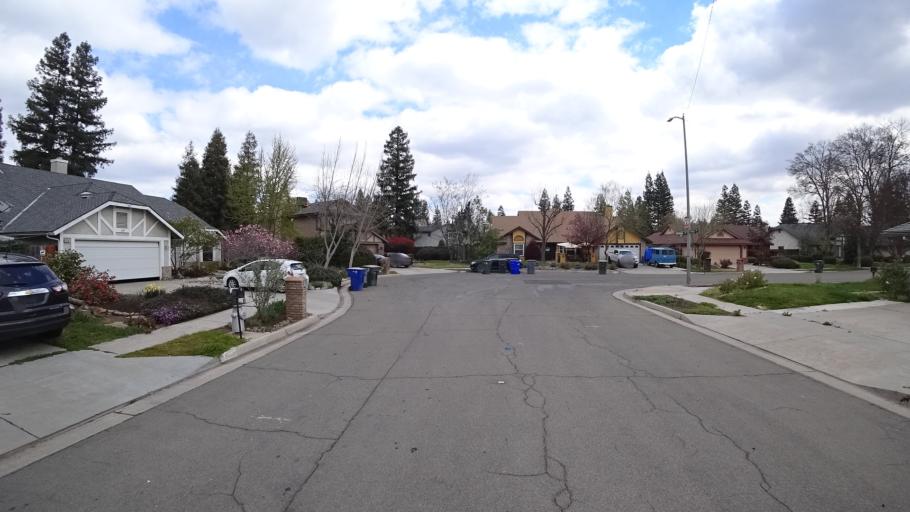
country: US
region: California
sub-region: Fresno County
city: Fresno
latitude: 36.8317
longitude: -119.8157
